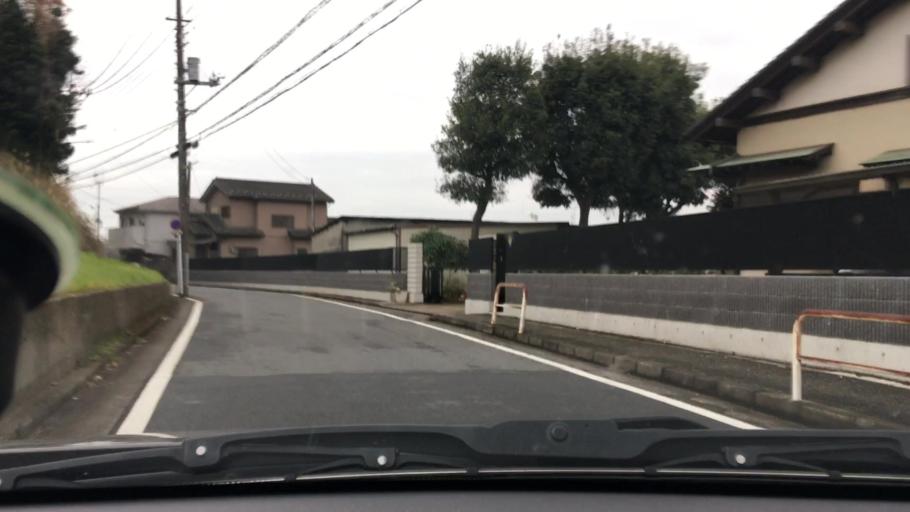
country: JP
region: Kanagawa
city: Yokohama
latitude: 35.5203
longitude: 139.6036
